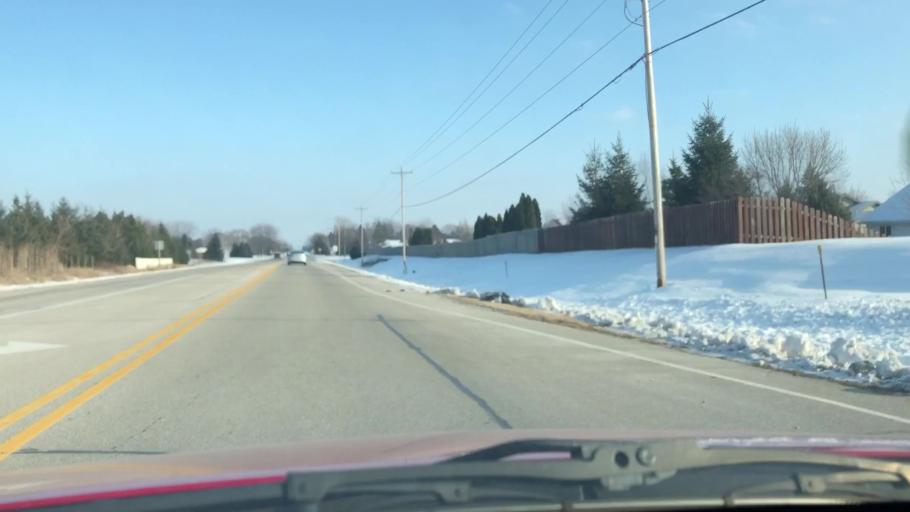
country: US
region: Wisconsin
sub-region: Outagamie County
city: Appleton
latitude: 44.3163
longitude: -88.4029
